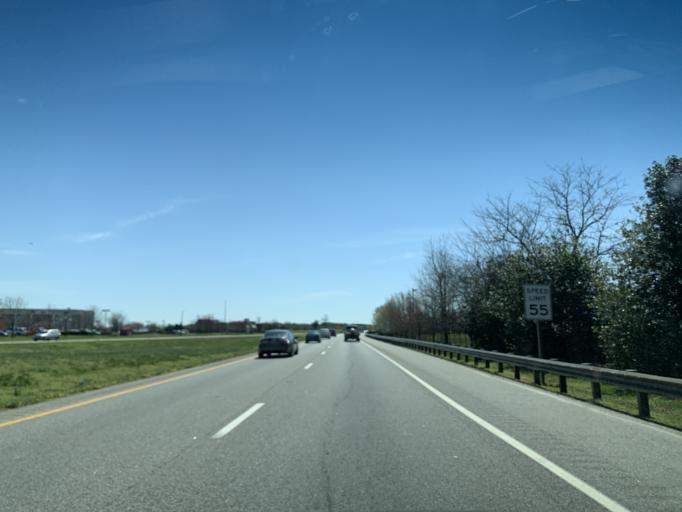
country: US
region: Maryland
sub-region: Talbot County
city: Easton
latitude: 38.7972
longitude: -76.0608
